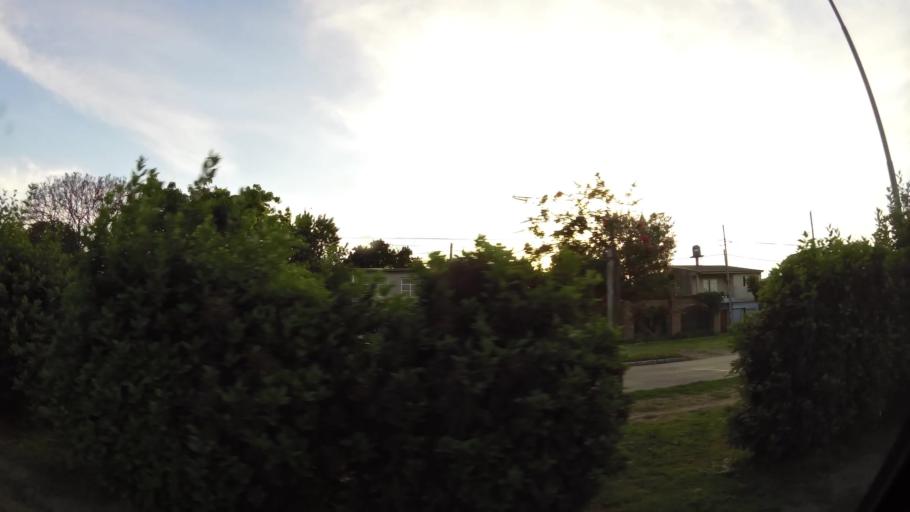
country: AR
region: Buenos Aires
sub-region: Partido de Quilmes
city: Quilmes
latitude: -34.7743
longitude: -58.2291
